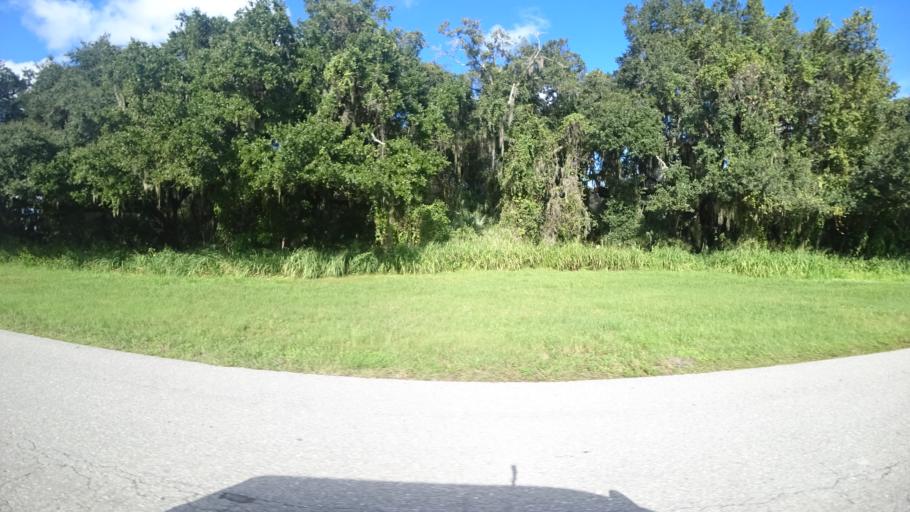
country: US
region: Florida
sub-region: Manatee County
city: Ellenton
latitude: 27.5733
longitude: -82.4751
